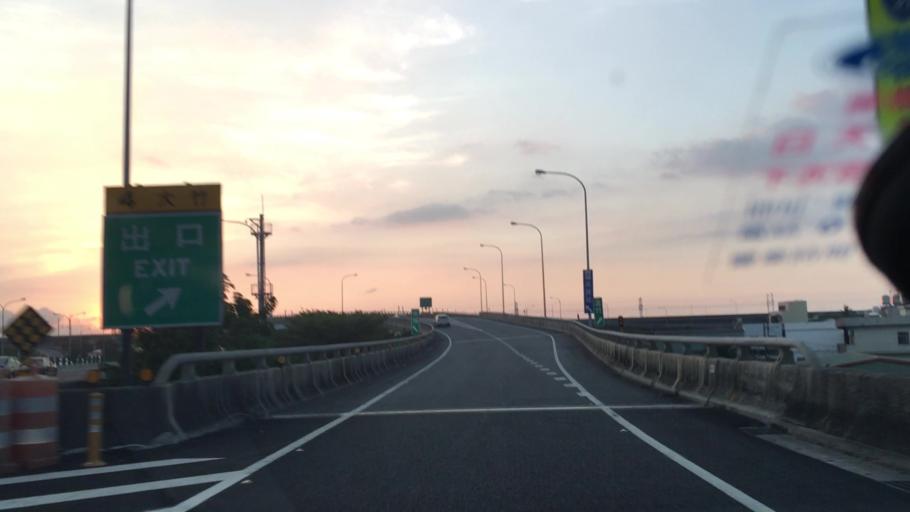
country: TW
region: Taiwan
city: Taoyuan City
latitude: 25.0336
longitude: 121.2420
